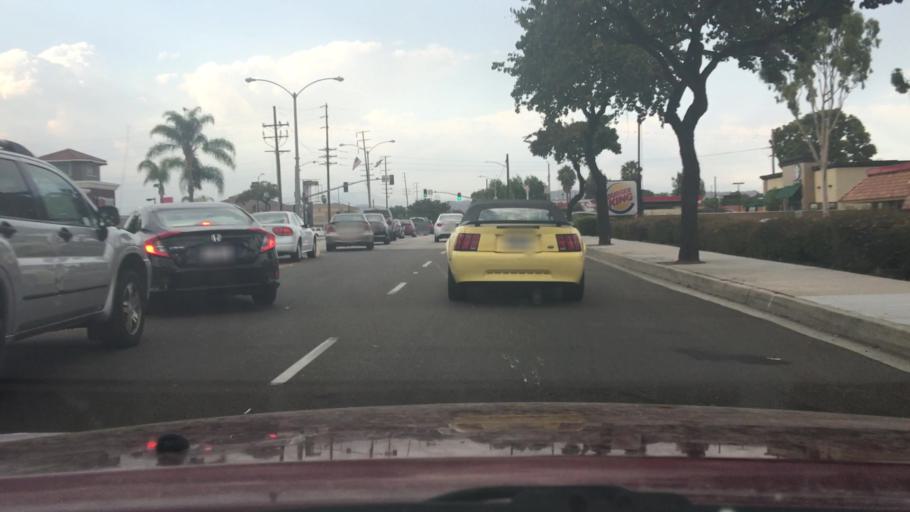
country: US
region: California
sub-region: Los Angeles County
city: La Mirada
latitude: 33.9159
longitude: -118.0118
